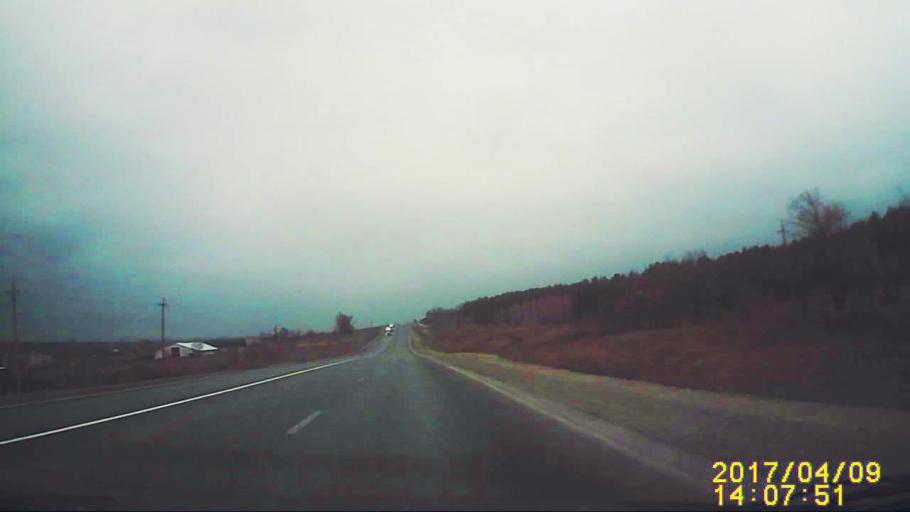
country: RU
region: Ulyanovsk
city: Silikatnyy
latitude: 54.0151
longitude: 48.2170
